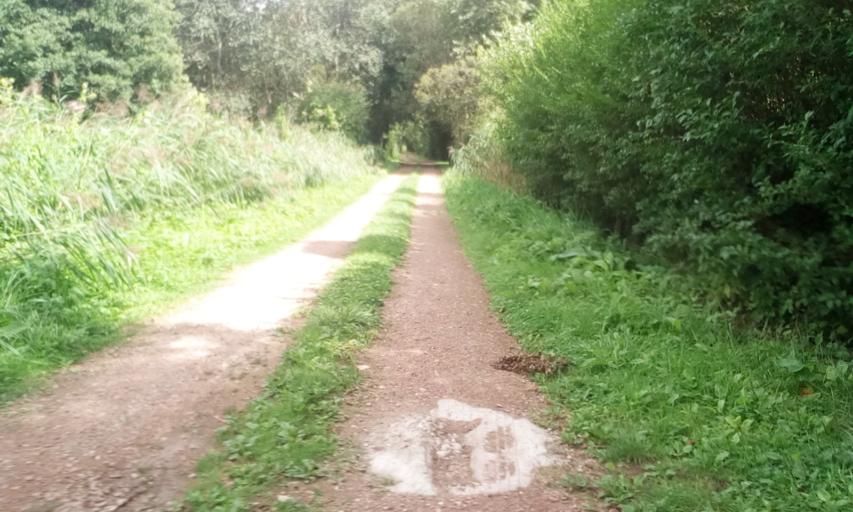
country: FR
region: Lower Normandy
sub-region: Departement du Calvados
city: Bellengreville
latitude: 49.1147
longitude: -0.2228
